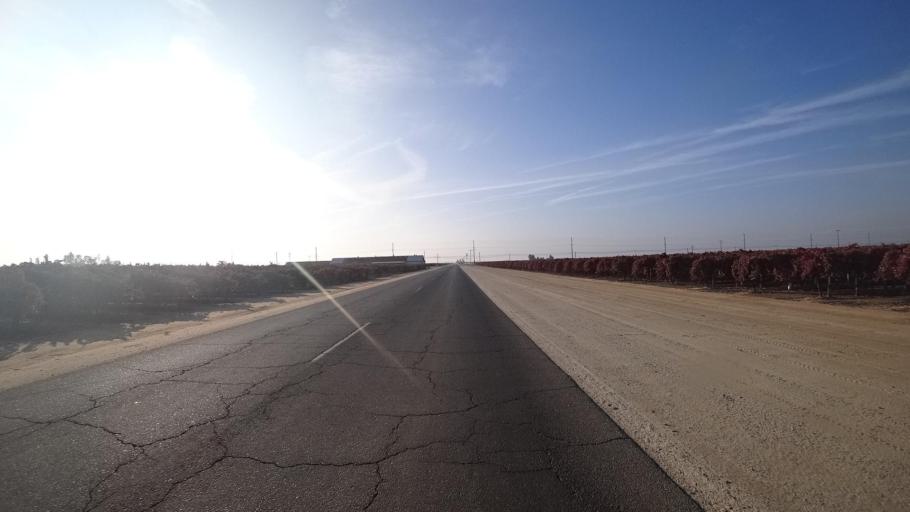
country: US
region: California
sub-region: Kern County
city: Delano
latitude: 35.7783
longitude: -119.1874
